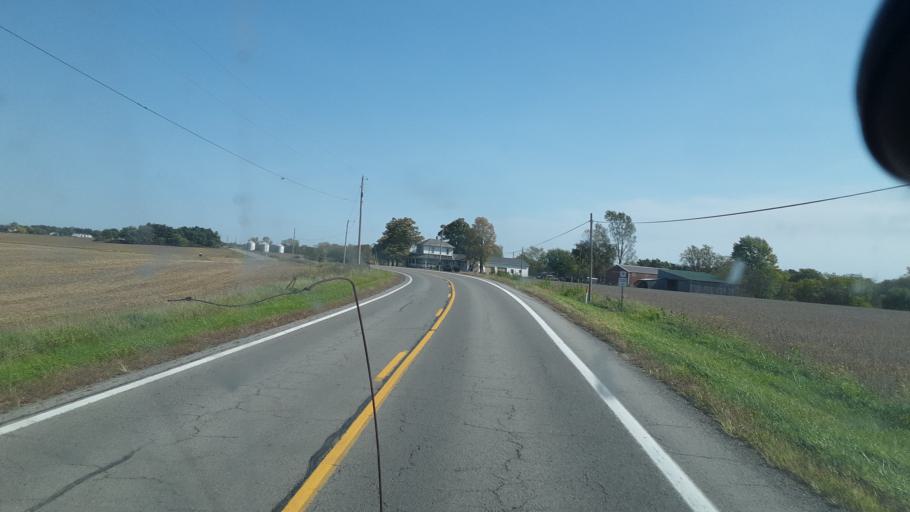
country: US
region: Ohio
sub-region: Logan County
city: Northwood
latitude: 40.5035
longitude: -83.7126
